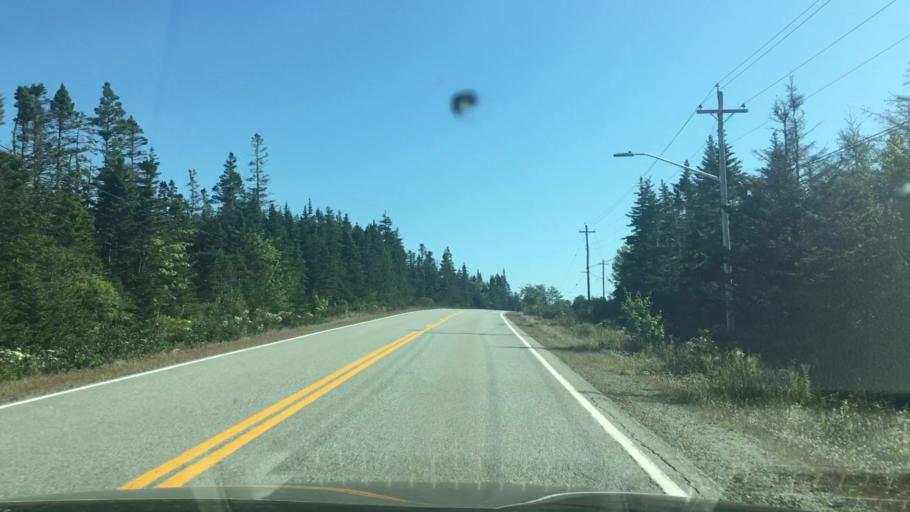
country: CA
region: Nova Scotia
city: Cole Harbour
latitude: 44.7783
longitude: -62.7831
